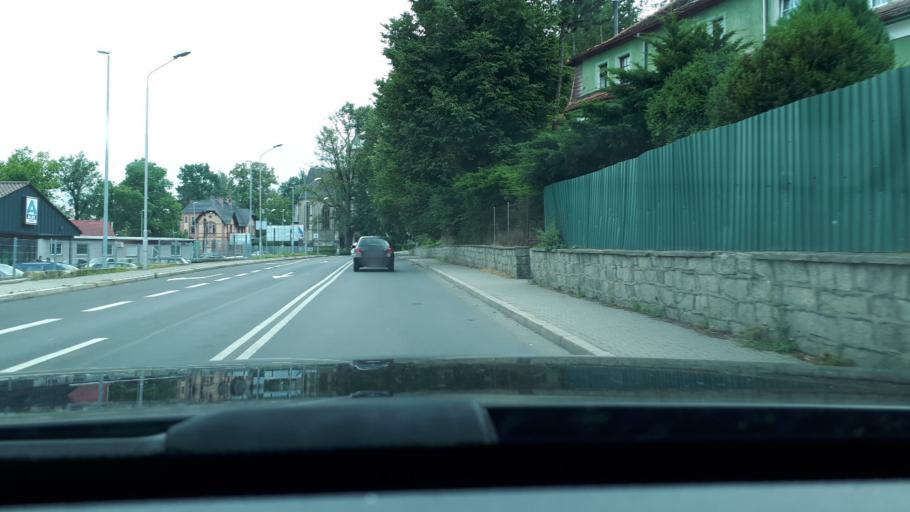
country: PL
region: Lower Silesian Voivodeship
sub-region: Powiat lubanski
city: Luban
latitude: 51.1166
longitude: 15.2895
